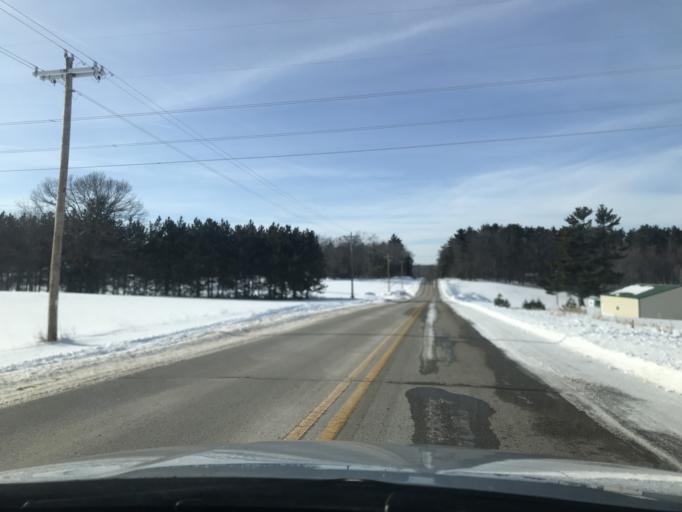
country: US
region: Wisconsin
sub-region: Oconto County
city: Oconto Falls
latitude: 45.1476
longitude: -88.1812
